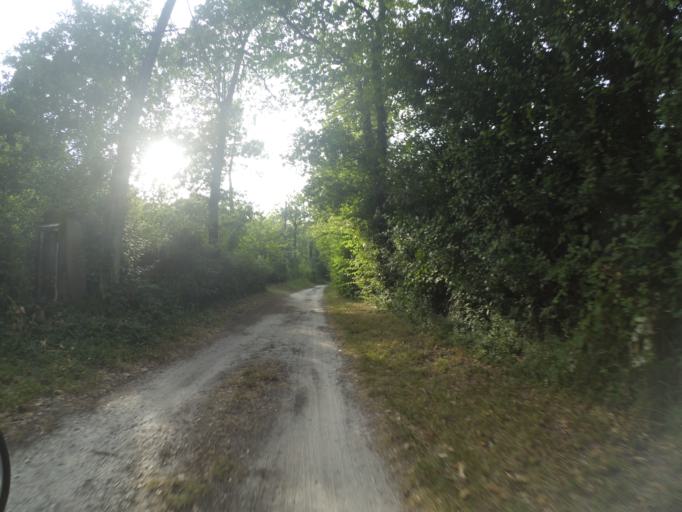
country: FR
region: Poitou-Charentes
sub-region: Departement de la Charente-Maritime
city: Meschers-sur-Gironde
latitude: 45.5770
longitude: -0.9738
